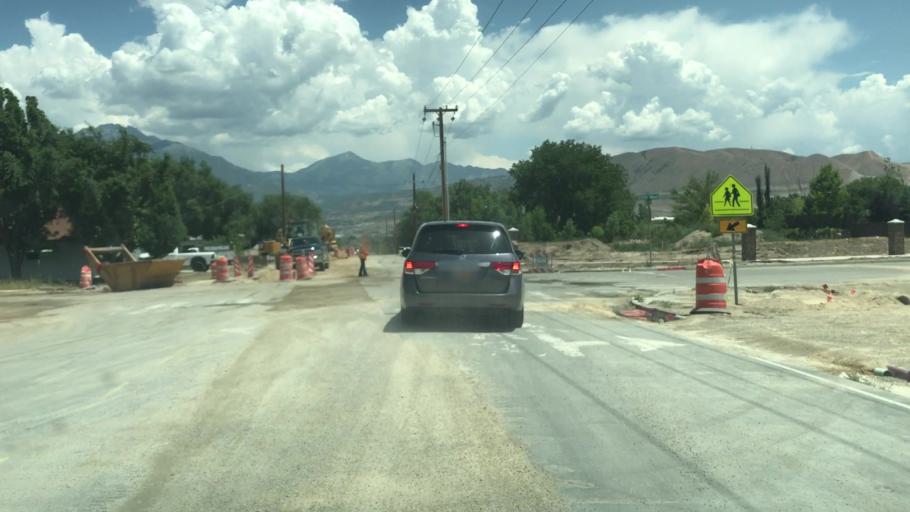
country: US
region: Utah
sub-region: Salt Lake County
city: Bluffdale
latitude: 40.4896
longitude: -111.9488
